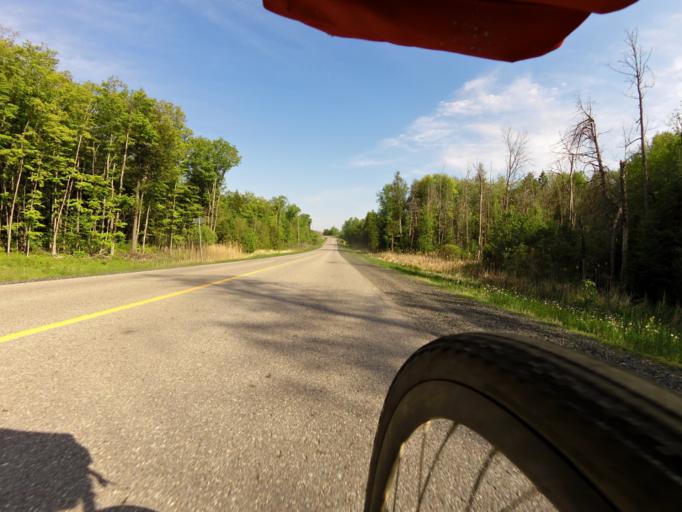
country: CA
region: Ontario
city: Arnprior
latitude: 45.1692
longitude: -76.4874
